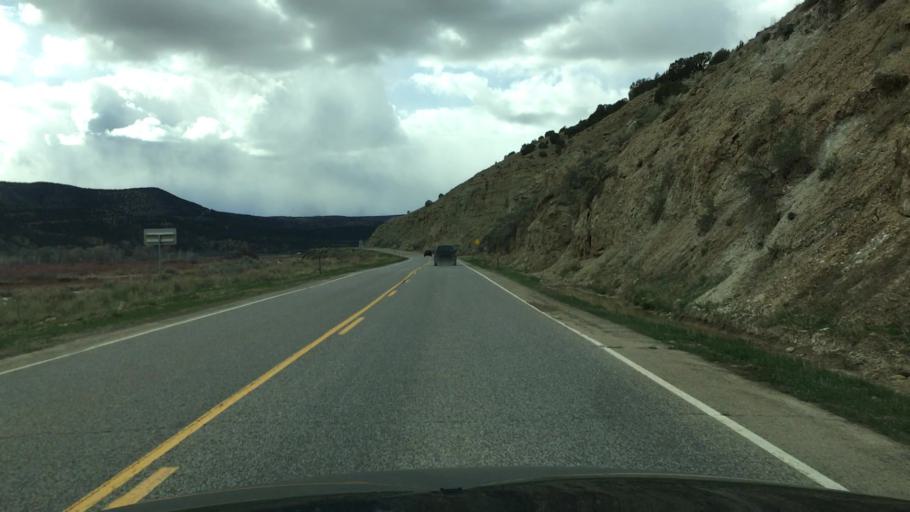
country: US
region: Colorado
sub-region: Rio Blanco County
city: Meeker
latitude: 40.0959
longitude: -108.2259
